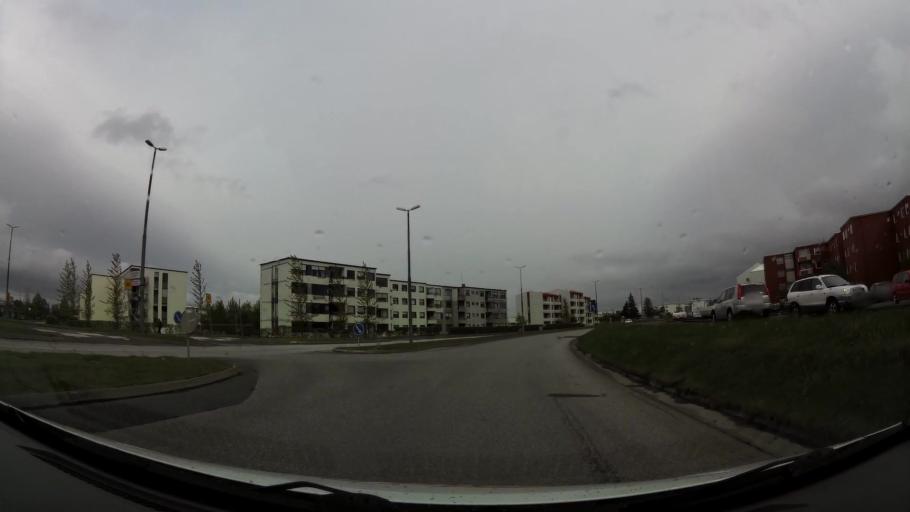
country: IS
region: Capital Region
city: Hafnarfjoerdur
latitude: 64.0795
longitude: -21.9619
